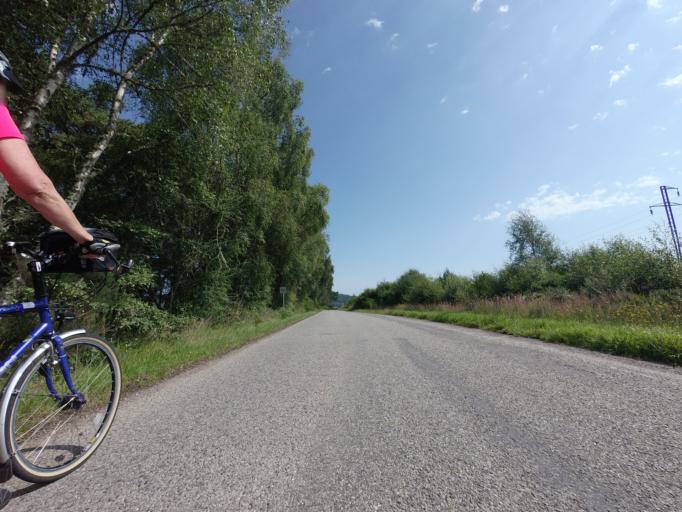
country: GB
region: Scotland
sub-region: Highland
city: Invergordon
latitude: 57.7436
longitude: -4.1758
